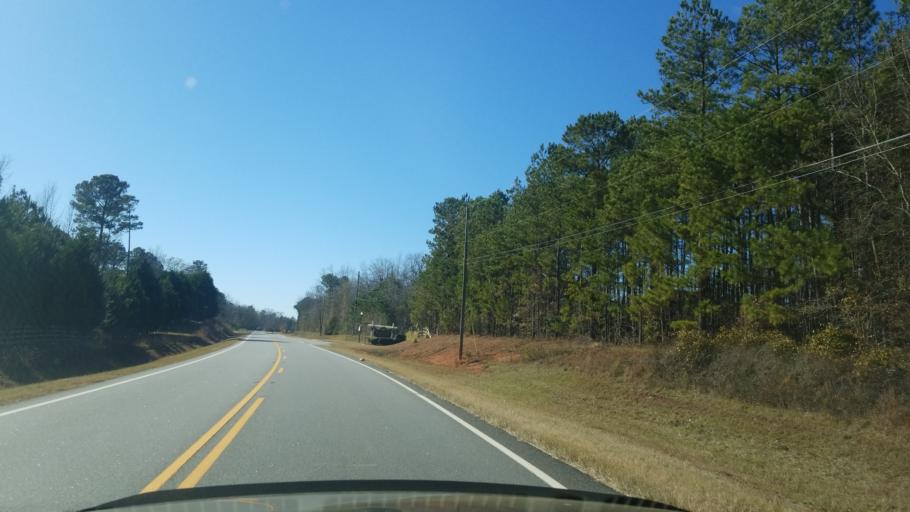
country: US
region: Georgia
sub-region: Harris County
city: Hamilton
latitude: 32.6314
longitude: -84.7644
